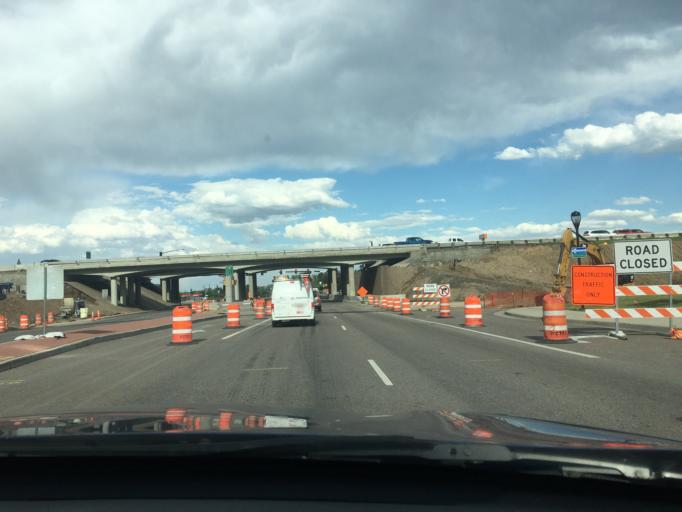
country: US
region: Colorado
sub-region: Jefferson County
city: Applewood
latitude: 39.7618
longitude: -105.1443
